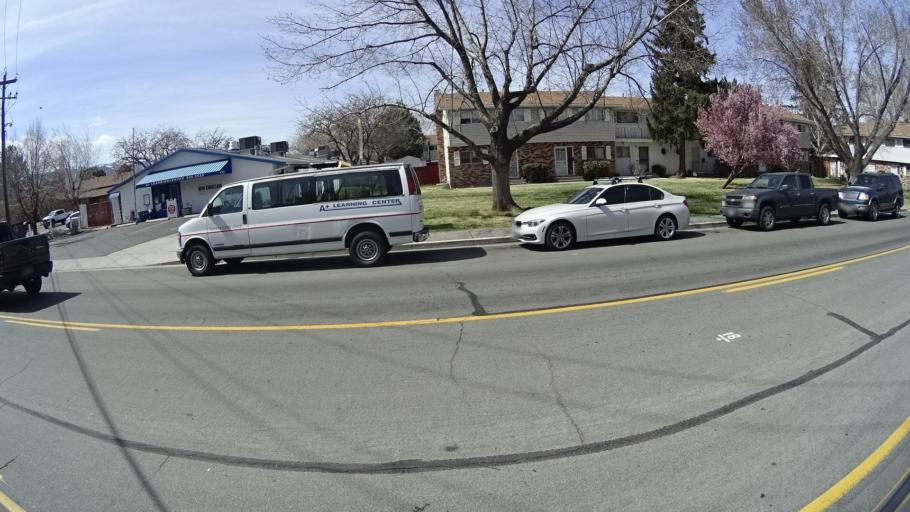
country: US
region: Nevada
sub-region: Washoe County
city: Reno
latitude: 39.4814
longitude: -119.7819
